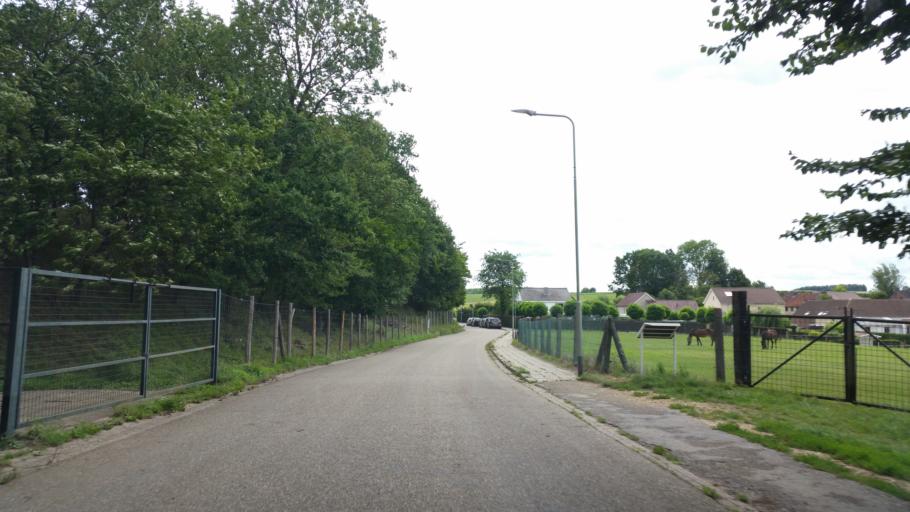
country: NL
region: Limburg
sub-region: Valkenburg aan de Geul
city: Berg
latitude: 50.8572
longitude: 5.7900
